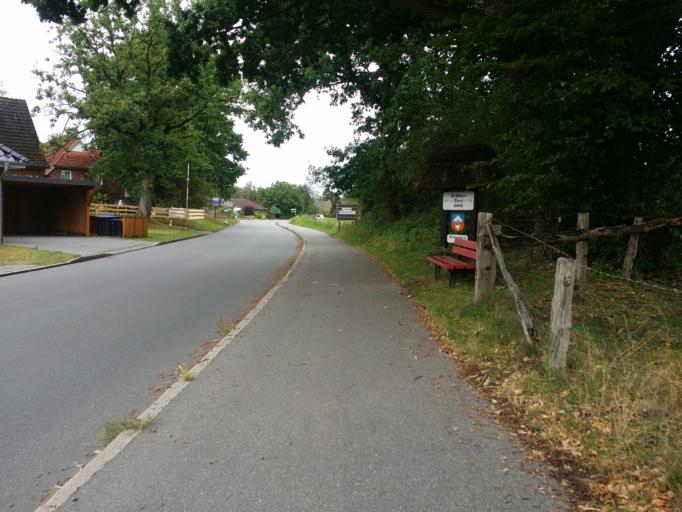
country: DE
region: Schleswig-Holstein
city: Oldendorf
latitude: 53.9451
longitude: 9.4659
